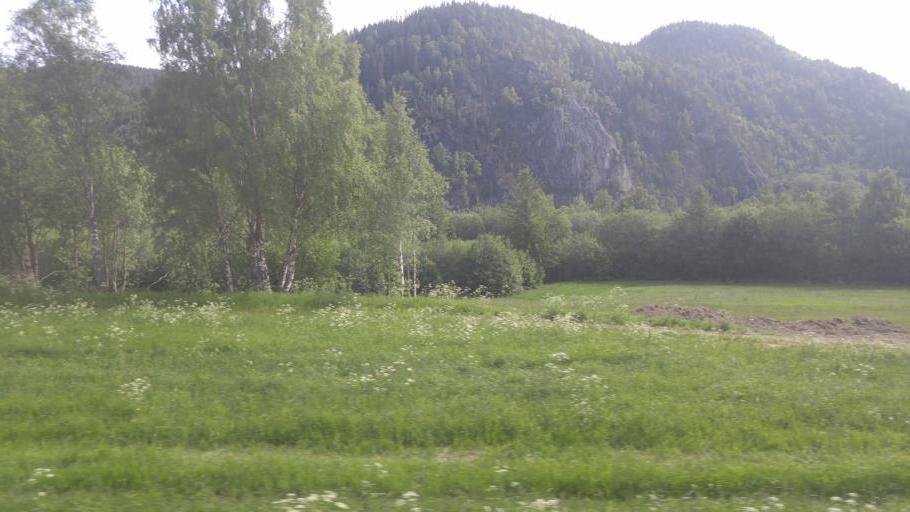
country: NO
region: Sor-Trondelag
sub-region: Midtre Gauldal
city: Storen
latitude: 63.0759
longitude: 10.2541
